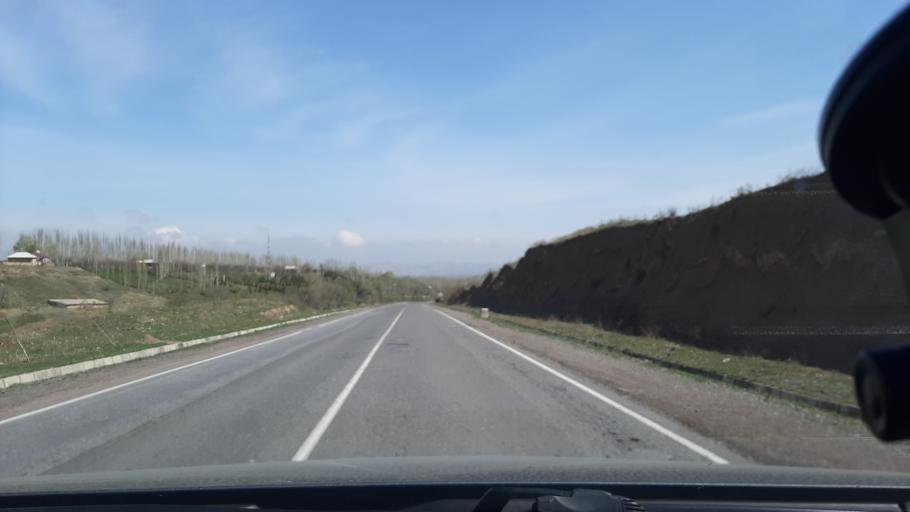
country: TJ
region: Viloyati Sughd
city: Shahriston
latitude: 39.7751
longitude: 68.8283
